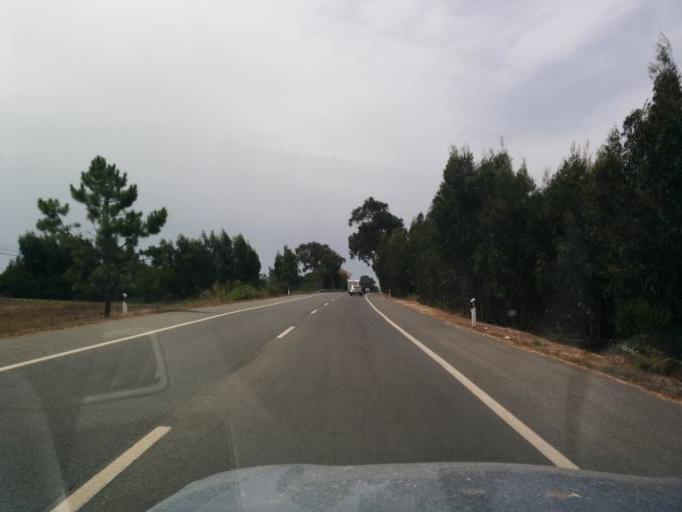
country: PT
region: Beja
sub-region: Odemira
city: Vila Nova de Milfontes
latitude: 37.7119
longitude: -8.7673
